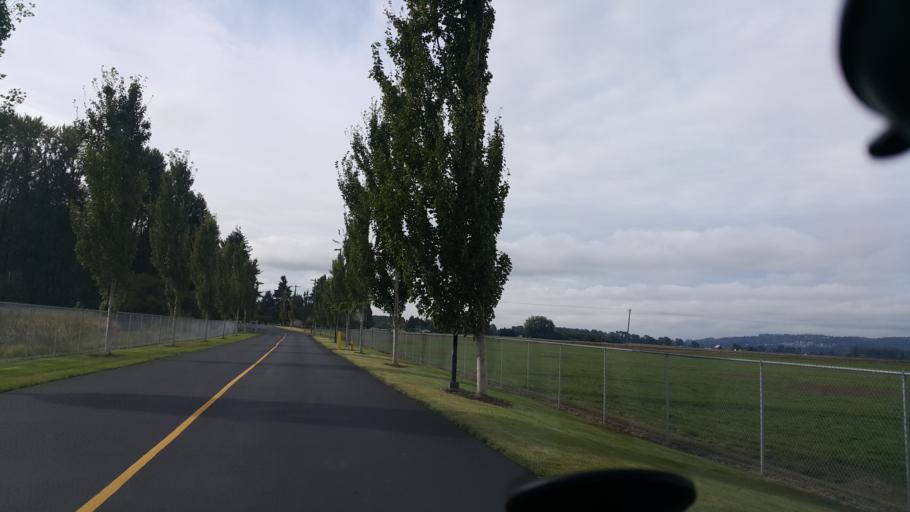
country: US
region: Washington
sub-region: Cowlitz County
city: Woodland
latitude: 45.9294
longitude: -122.7685
